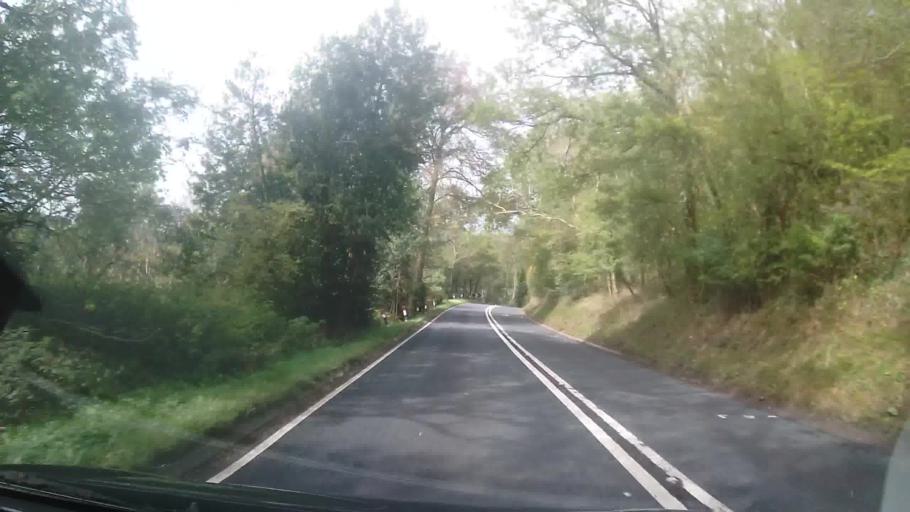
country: GB
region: England
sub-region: Worcestershire
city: Kidderminster
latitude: 52.4147
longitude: -2.2847
